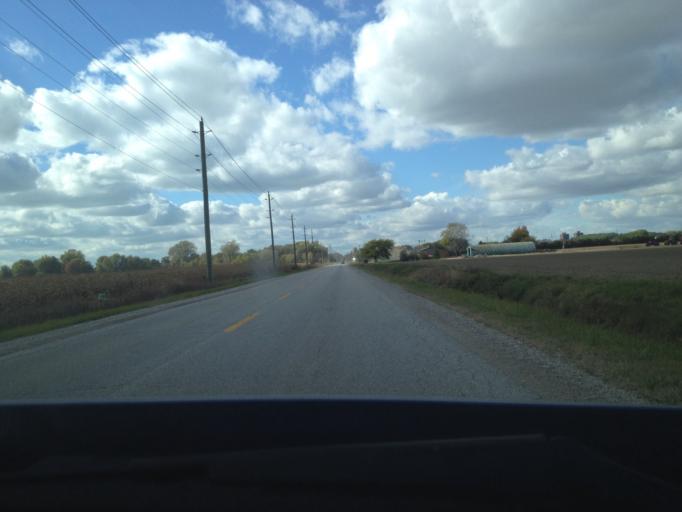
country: CA
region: Ontario
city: Amherstburg
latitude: 42.0329
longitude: -82.5736
